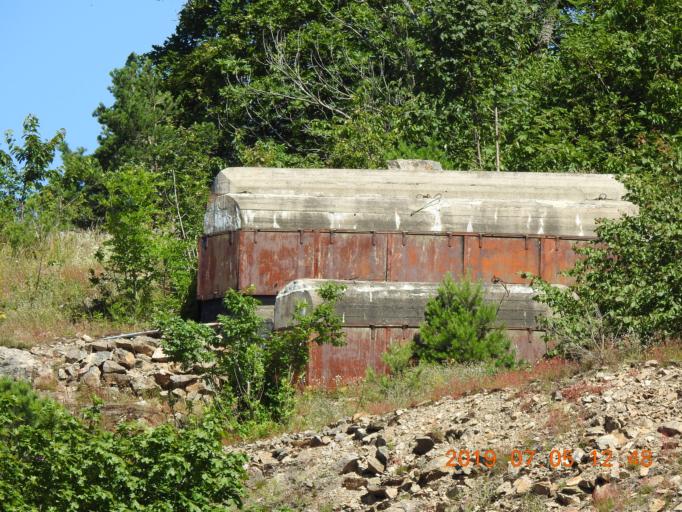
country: NO
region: Akershus
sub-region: Frogn
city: Drobak
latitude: 59.6702
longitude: 10.6228
